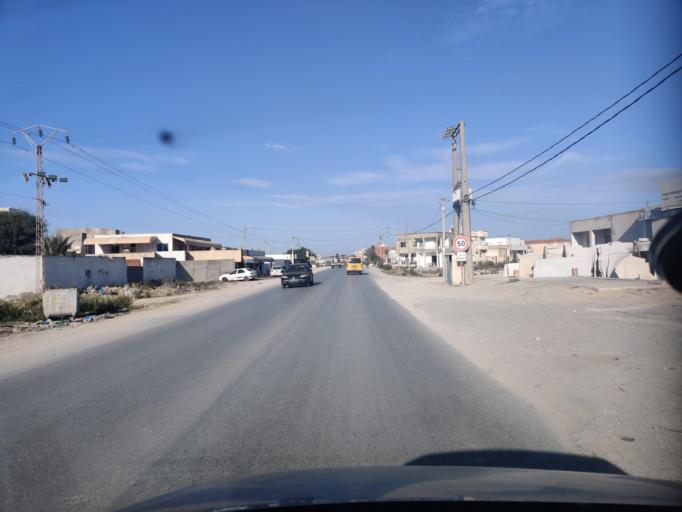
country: TN
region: Ariana
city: Ariana
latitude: 36.9564
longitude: 10.2113
